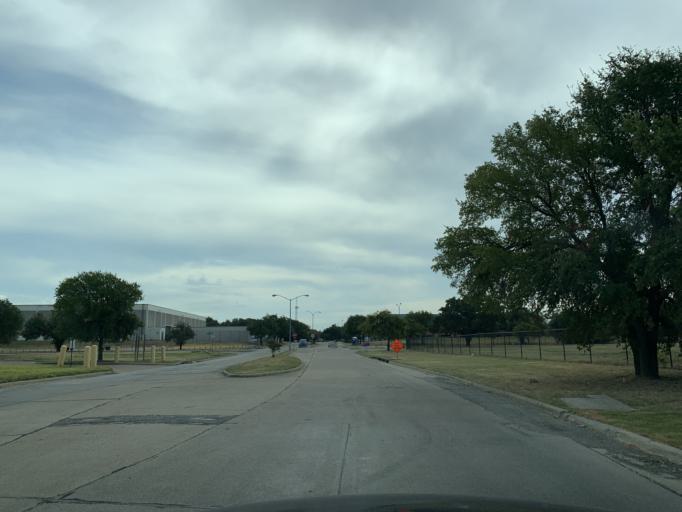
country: US
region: Texas
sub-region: Dallas County
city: Cockrell Hill
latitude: 32.7688
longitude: -96.8638
